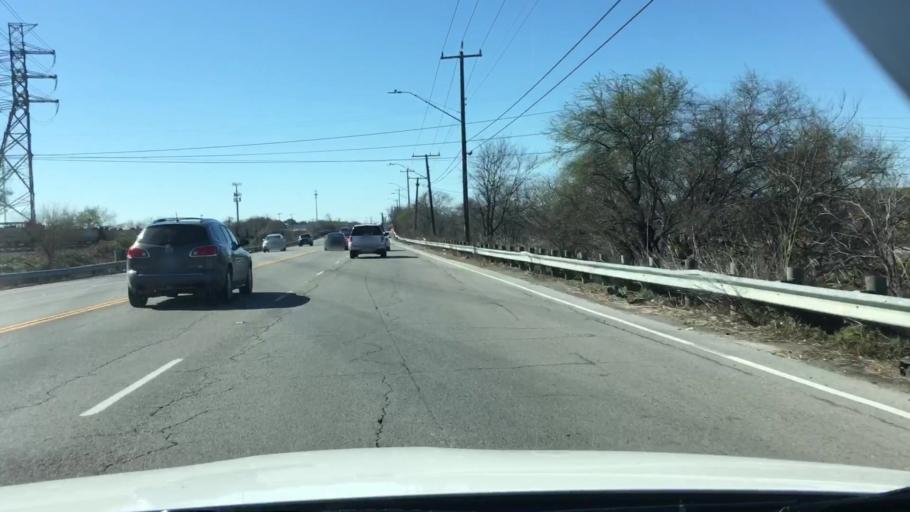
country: US
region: Texas
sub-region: Bexar County
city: Alamo Heights
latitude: 29.5436
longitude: -98.4400
